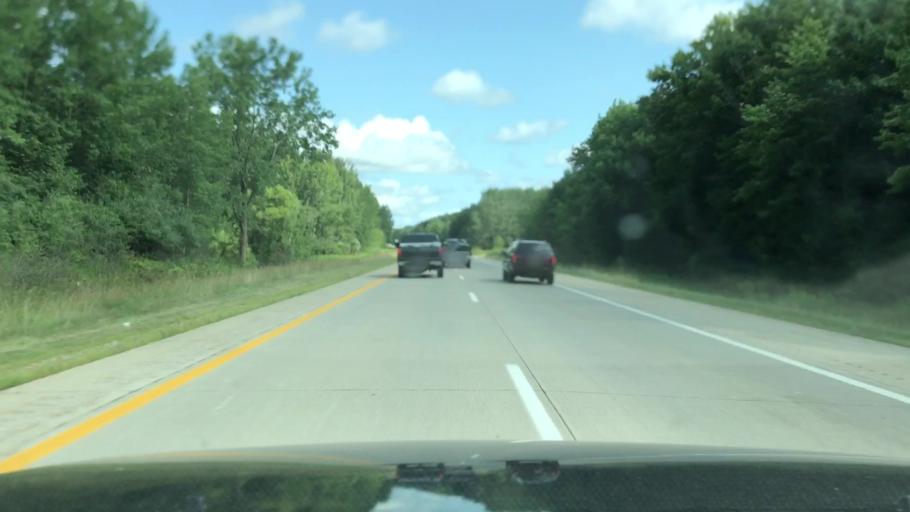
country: US
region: Michigan
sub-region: Montcalm County
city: Howard City
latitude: 43.3497
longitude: -85.5100
